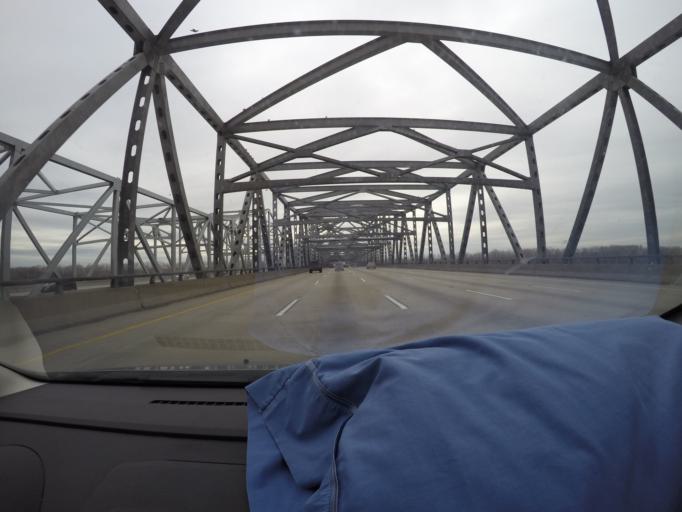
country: US
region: Missouri
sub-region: Saint Charles County
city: Saint Charles
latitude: 38.7648
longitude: -90.4845
